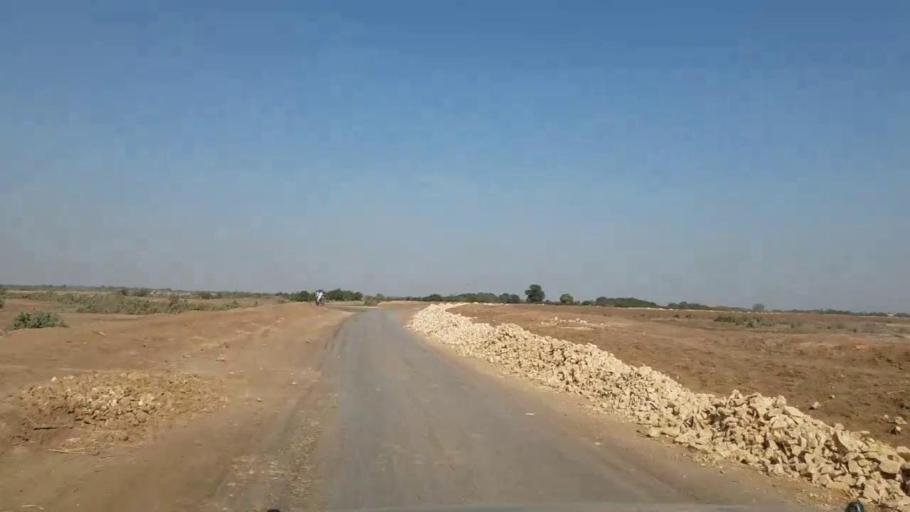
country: PK
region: Sindh
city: Digri
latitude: 24.9711
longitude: 69.1136
